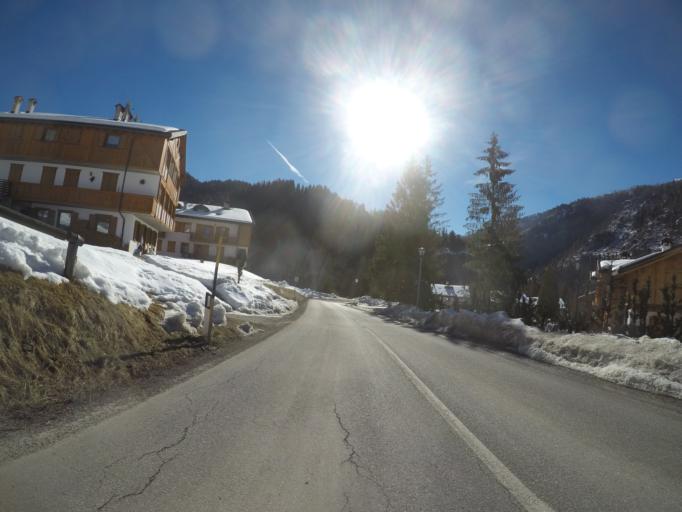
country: IT
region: Veneto
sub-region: Provincia di Belluno
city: Colle Santa Lucia
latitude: 46.4392
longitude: 11.9991
